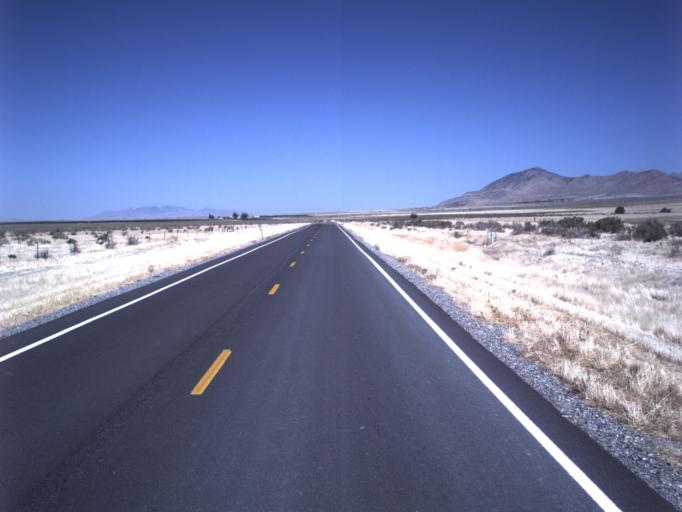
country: US
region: Utah
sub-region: Tooele County
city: Grantsville
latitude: 40.4623
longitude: -112.7472
